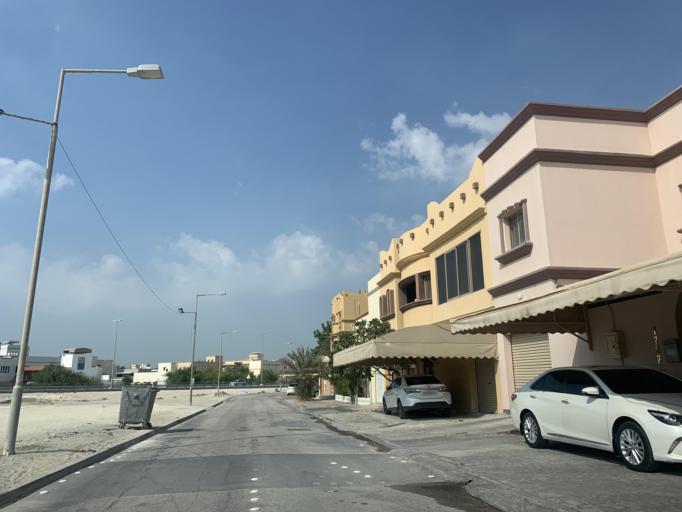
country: BH
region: Central Governorate
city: Madinat Hamad
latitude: 26.1039
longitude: 50.4991
